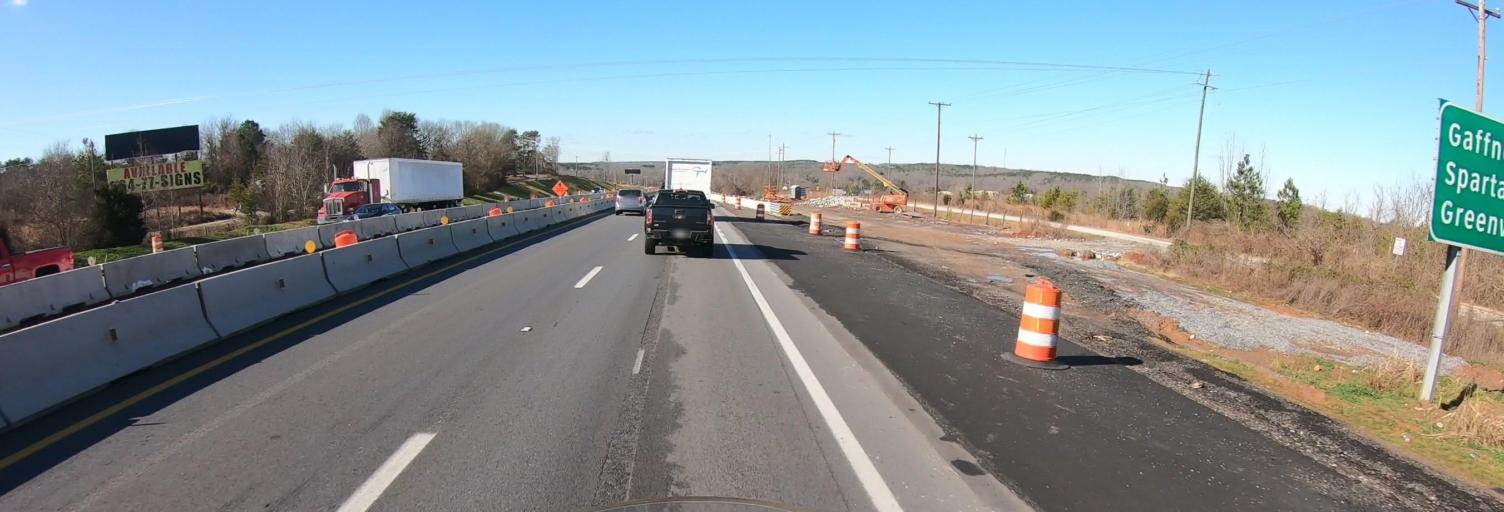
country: US
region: South Carolina
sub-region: Cherokee County
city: Blacksburg
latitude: 35.1367
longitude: -81.5239
